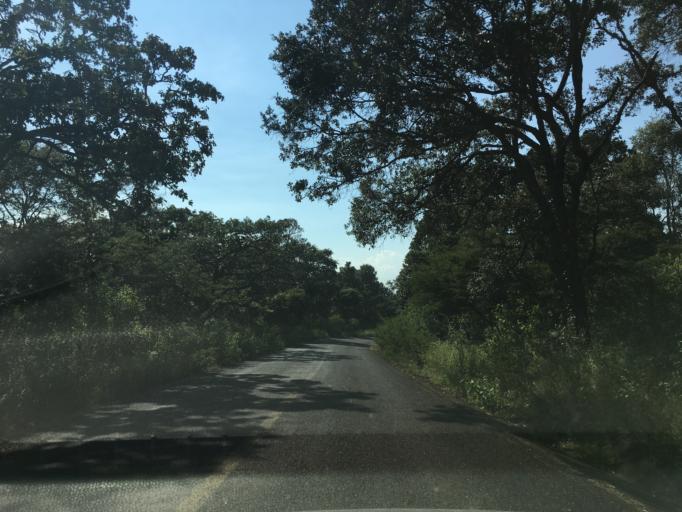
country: MX
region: Michoacan
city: Acuitzio del Canje
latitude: 19.5458
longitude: -101.2587
